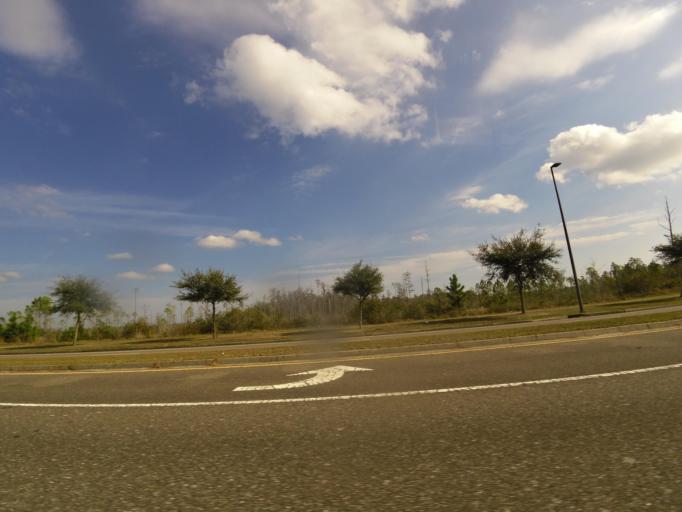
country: US
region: Florida
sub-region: Duval County
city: Baldwin
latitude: 30.2647
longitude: -81.8867
